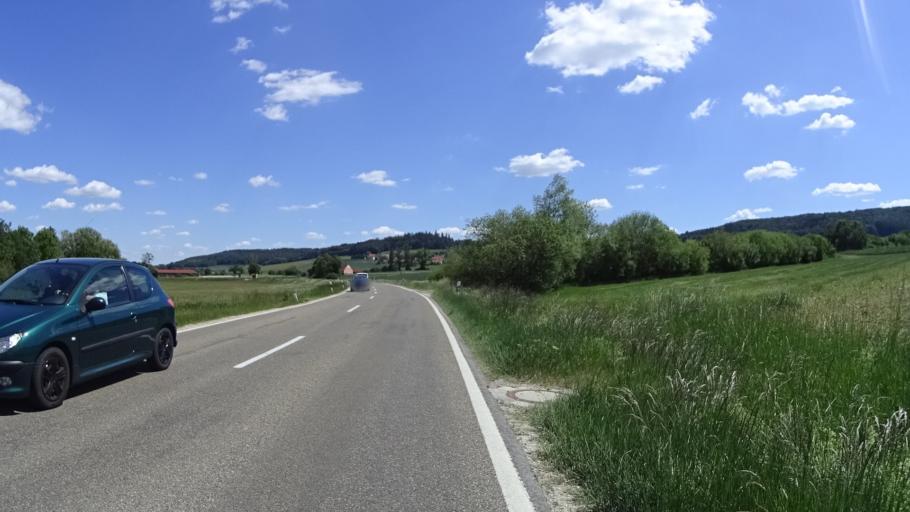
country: DE
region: Bavaria
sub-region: Regierungsbezirk Mittelfranken
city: Thalmassing
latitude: 49.0842
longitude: 11.2404
